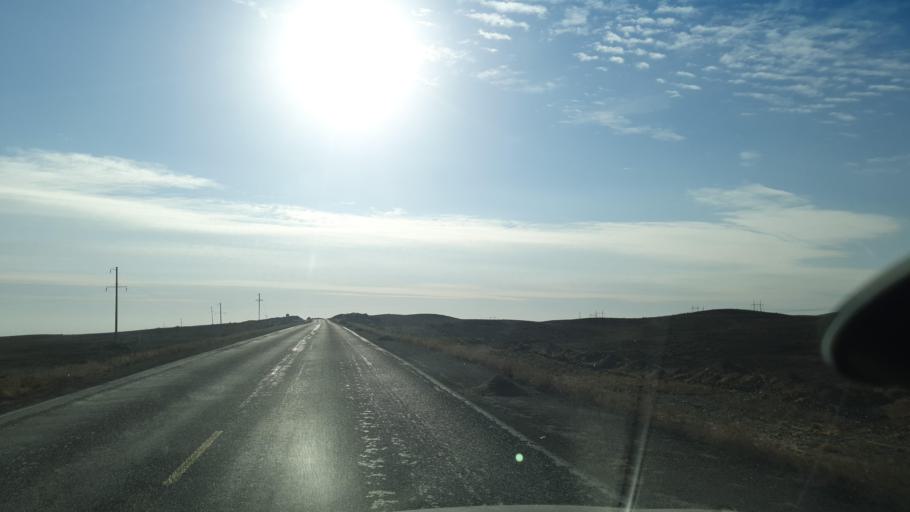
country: KZ
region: Zhambyl
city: Mynaral
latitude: 45.7114
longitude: 73.4003
